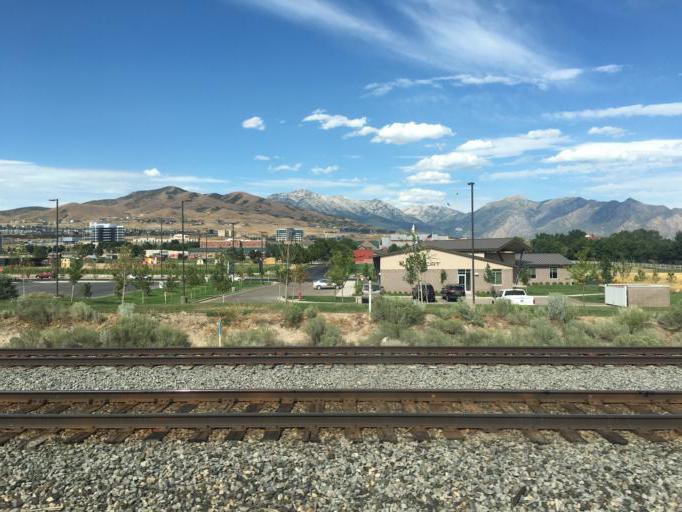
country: US
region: Utah
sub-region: Utah County
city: Lehi
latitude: 40.4218
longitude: -111.8925
